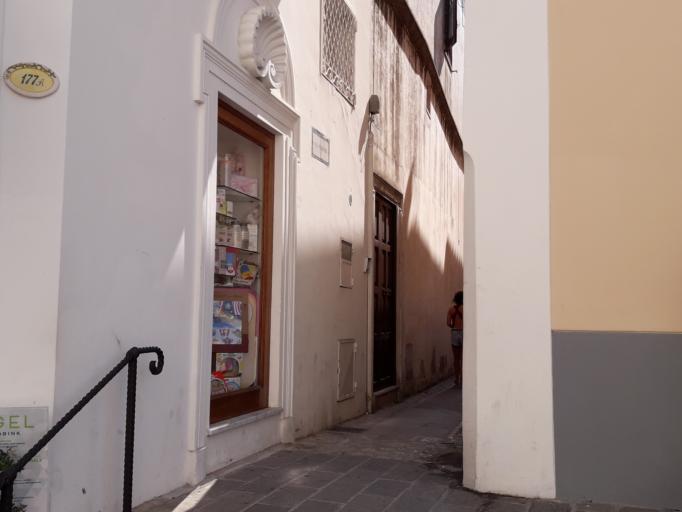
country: IT
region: Campania
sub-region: Provincia di Napoli
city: Anacapri
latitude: 40.5544
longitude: 14.2176
